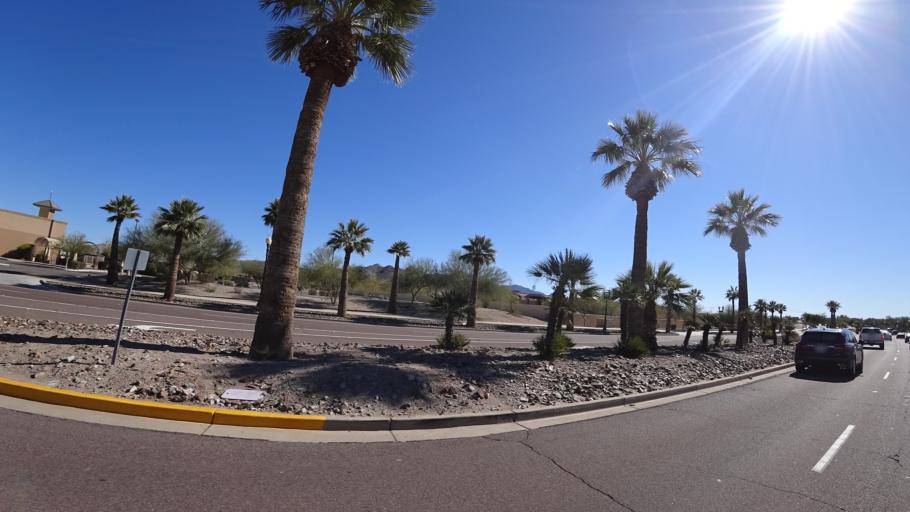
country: US
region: Arizona
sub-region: Maricopa County
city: Goodyear
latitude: 33.3508
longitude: -112.4285
